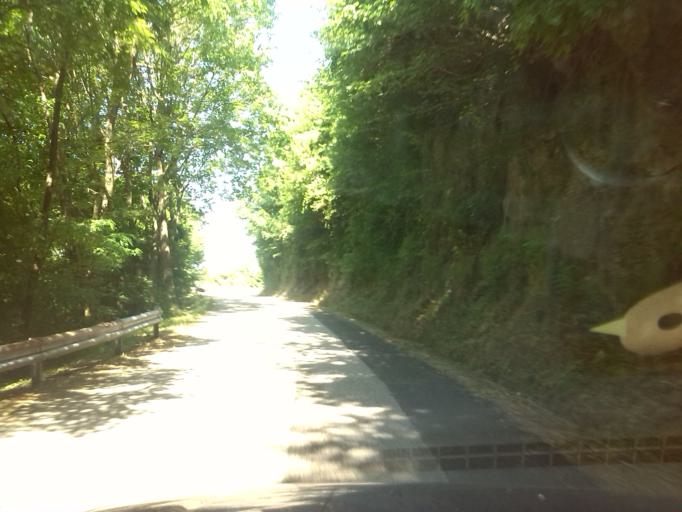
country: IT
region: Friuli Venezia Giulia
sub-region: Provincia di Udine
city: Clodig
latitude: 46.1377
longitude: 13.6160
